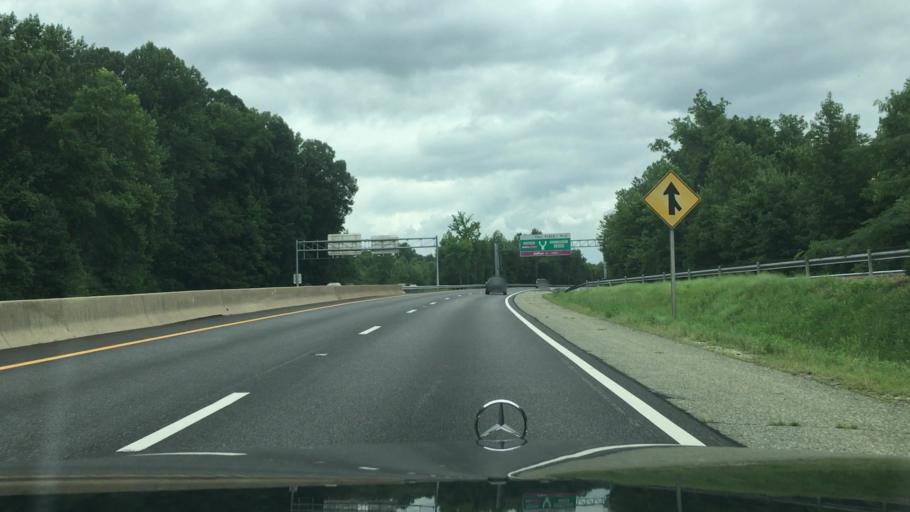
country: US
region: Virginia
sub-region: Chesterfield County
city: Bon Air
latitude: 37.5201
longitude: -77.5338
